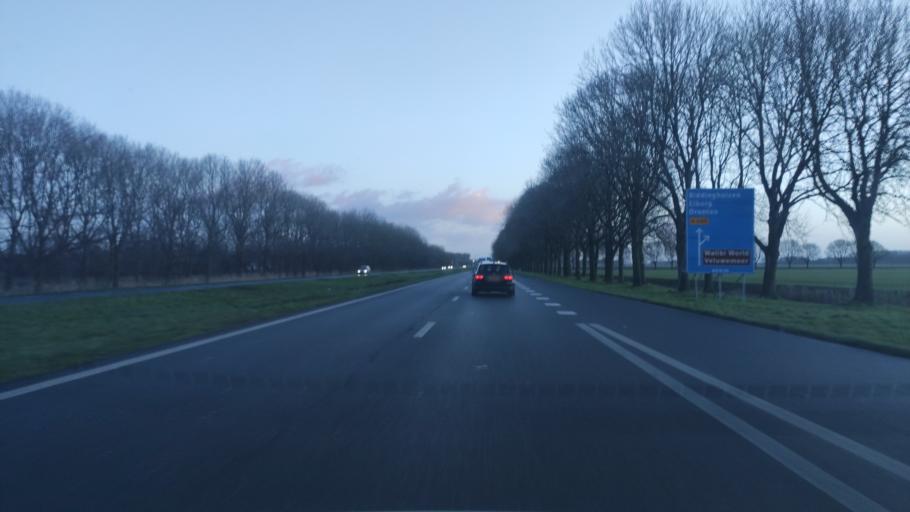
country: NL
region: Gelderland
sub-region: Gemeente Harderwijk
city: Harderwijk
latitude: 52.4019
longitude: 5.5865
